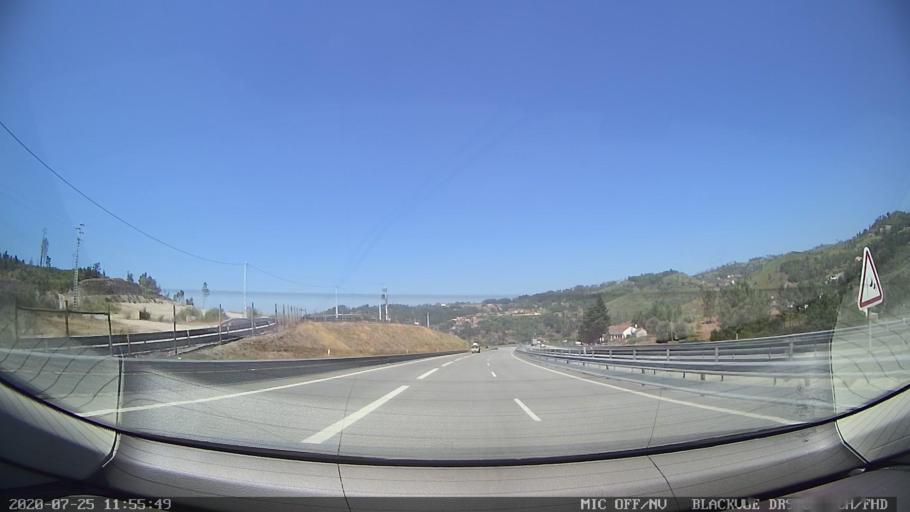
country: PT
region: Porto
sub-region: Amarante
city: Amarante
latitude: 41.2584
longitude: -8.0181
